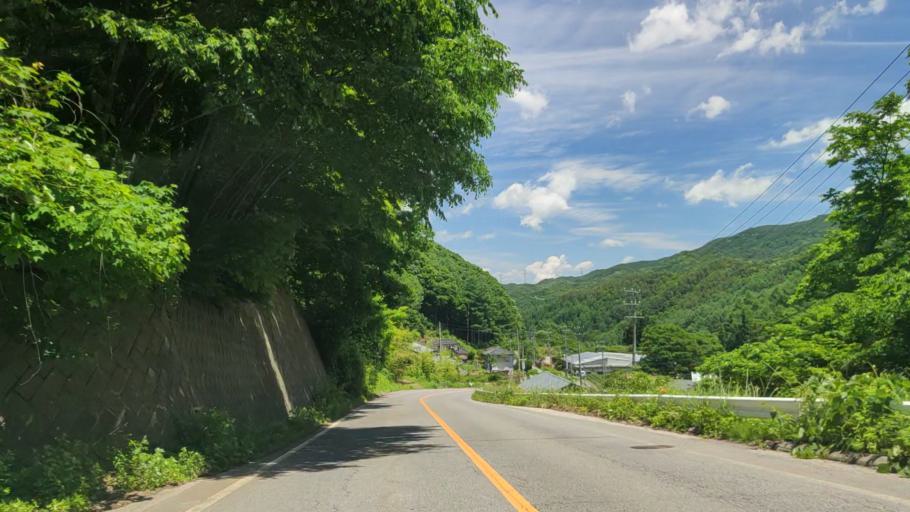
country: JP
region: Nagano
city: Kamimaruko
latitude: 36.1737
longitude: 138.2414
